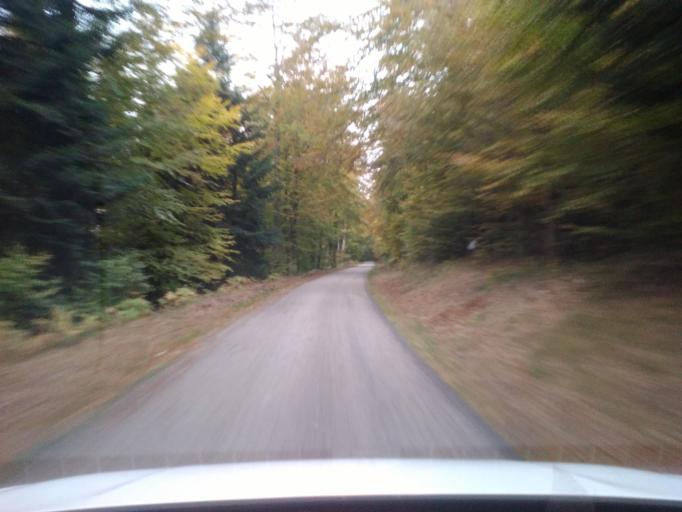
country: FR
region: Lorraine
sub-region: Departement des Vosges
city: Senones
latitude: 48.3794
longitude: 7.0882
